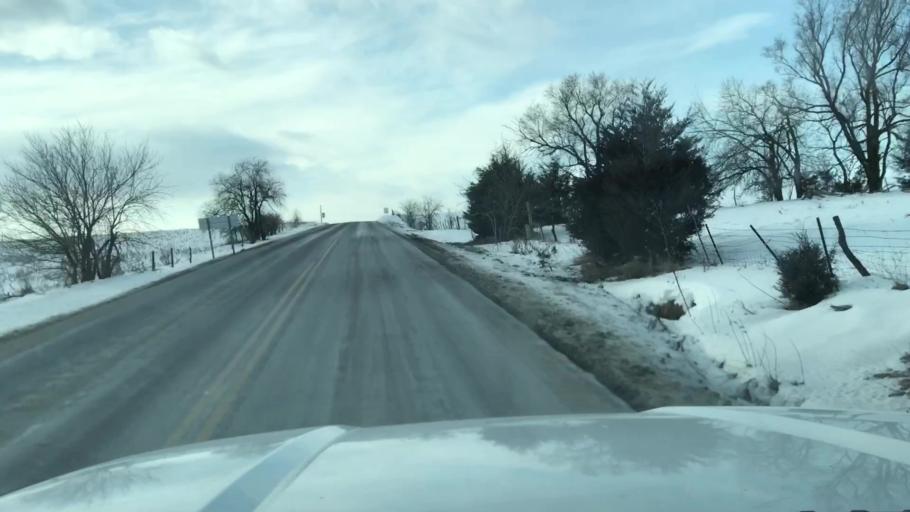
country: US
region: Missouri
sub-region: Nodaway County
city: Maryville
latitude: 40.2003
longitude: -94.8689
